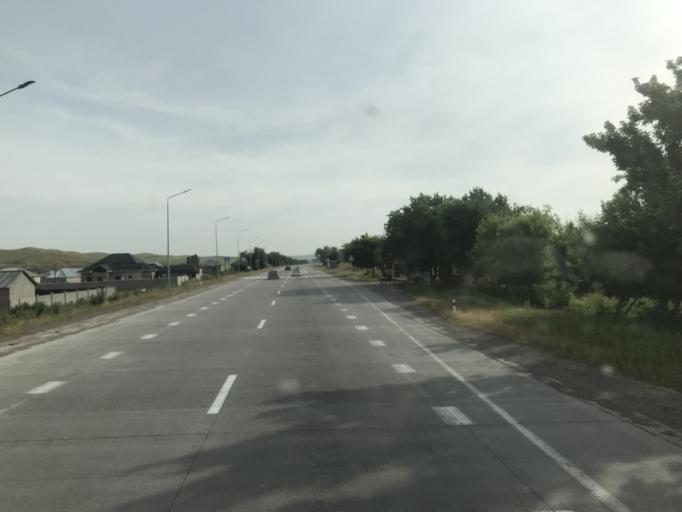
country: KZ
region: Ongtustik Qazaqstan
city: Qazyqurt
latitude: 41.9063
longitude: 69.4654
